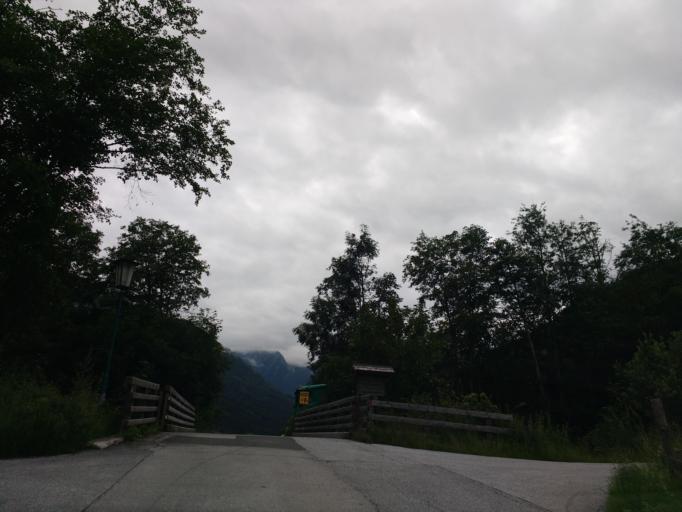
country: AT
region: Salzburg
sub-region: Politischer Bezirk Zell am See
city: Bramberg am Wildkogel
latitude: 47.2627
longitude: 12.3253
